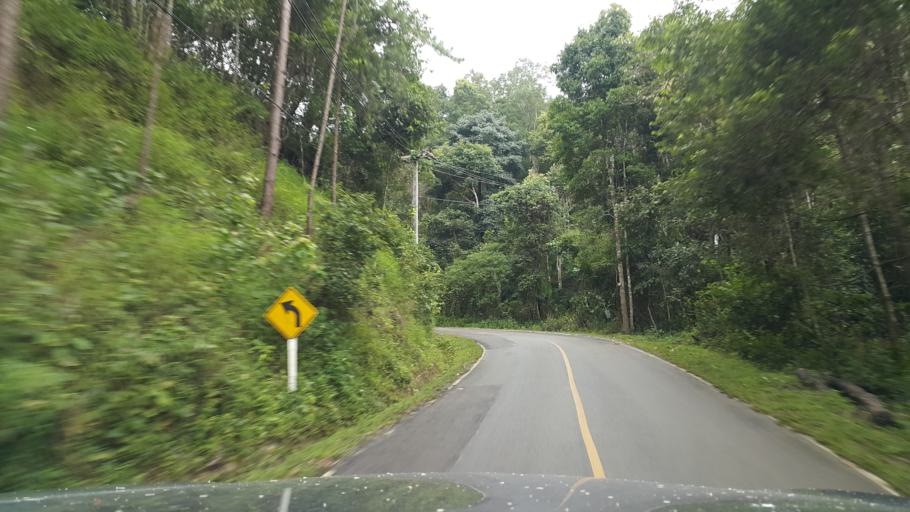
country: TH
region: Chiang Mai
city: Samoeng
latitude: 18.8835
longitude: 98.5262
